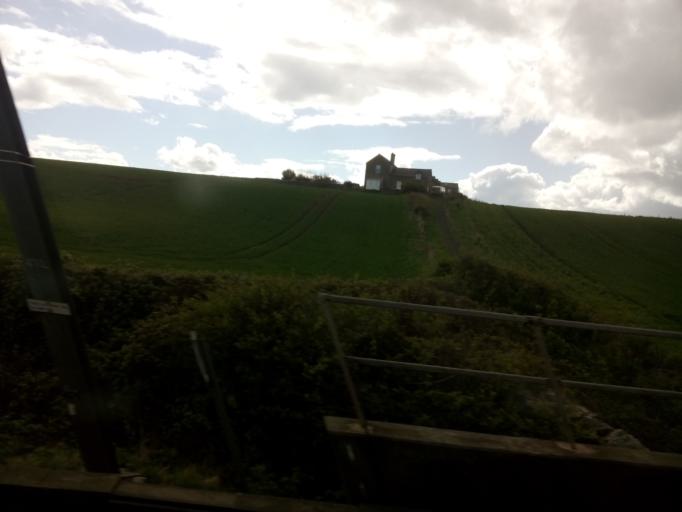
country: GB
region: England
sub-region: Northumberland
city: Berwick-Upon-Tweed
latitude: 55.7514
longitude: -1.9859
